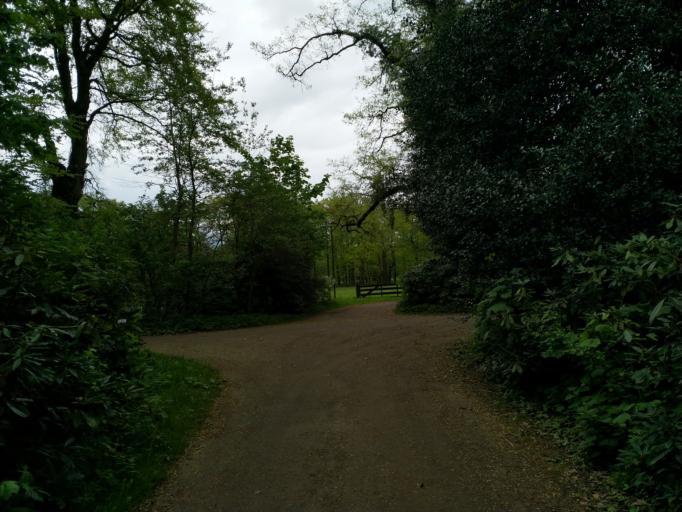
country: NL
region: Overijssel
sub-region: Gemeente Enschede
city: Enschede
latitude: 52.2351
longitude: 6.8692
